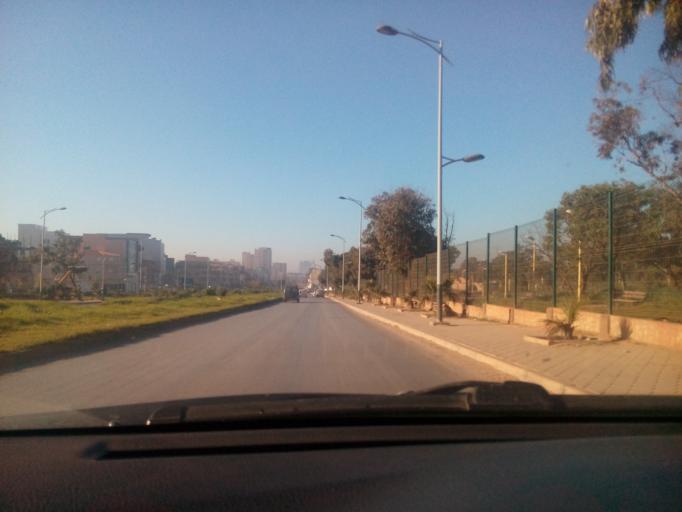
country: DZ
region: Oran
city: Bir el Djir
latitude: 35.7425
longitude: -0.5654
